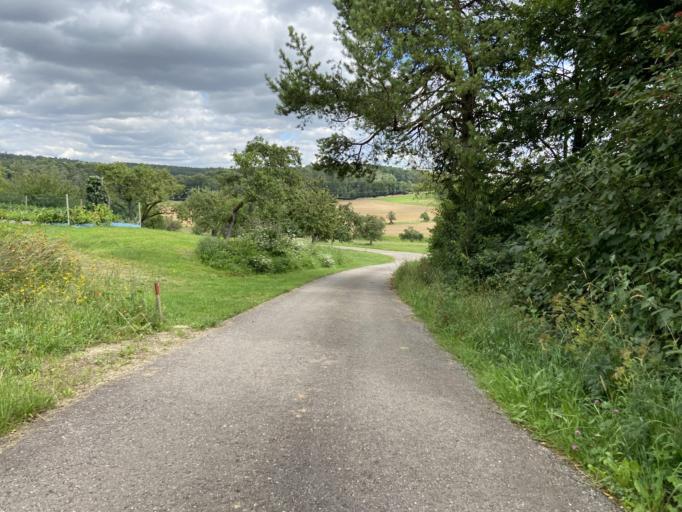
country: DE
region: Baden-Wuerttemberg
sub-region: Tuebingen Region
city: Bingen
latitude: 48.0998
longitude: 9.2957
